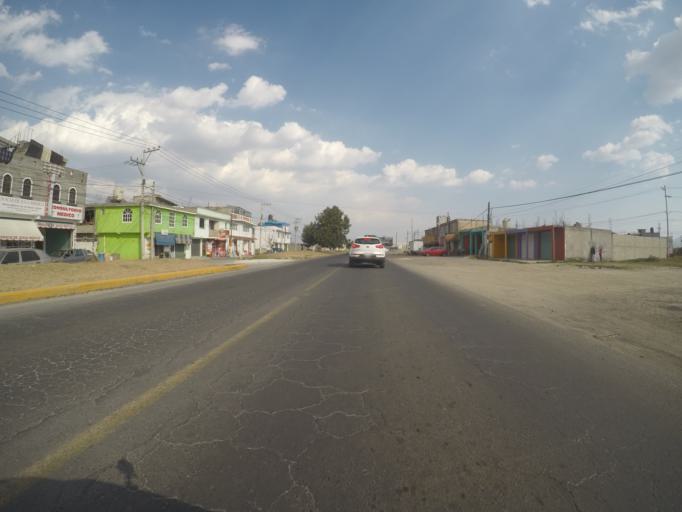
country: MX
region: Morelos
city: Chapultepec
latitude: 19.2015
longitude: -99.5489
